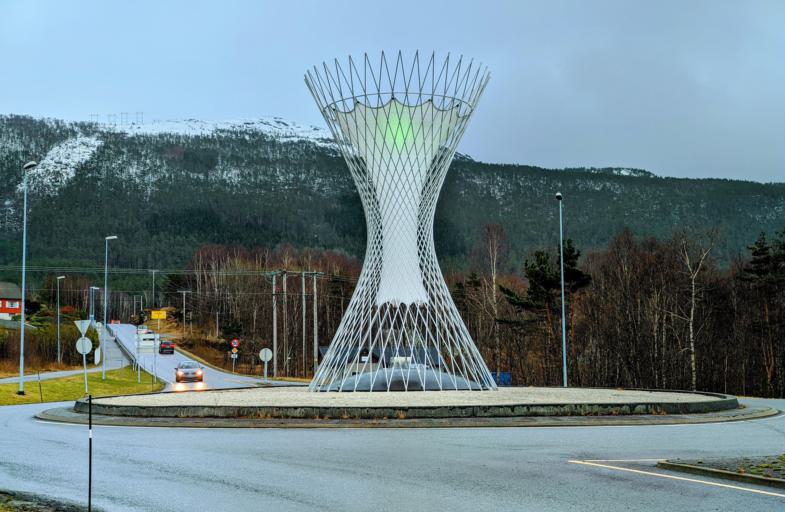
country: NO
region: Hordaland
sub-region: Etne
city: Etne
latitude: 59.8612
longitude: 5.7671
